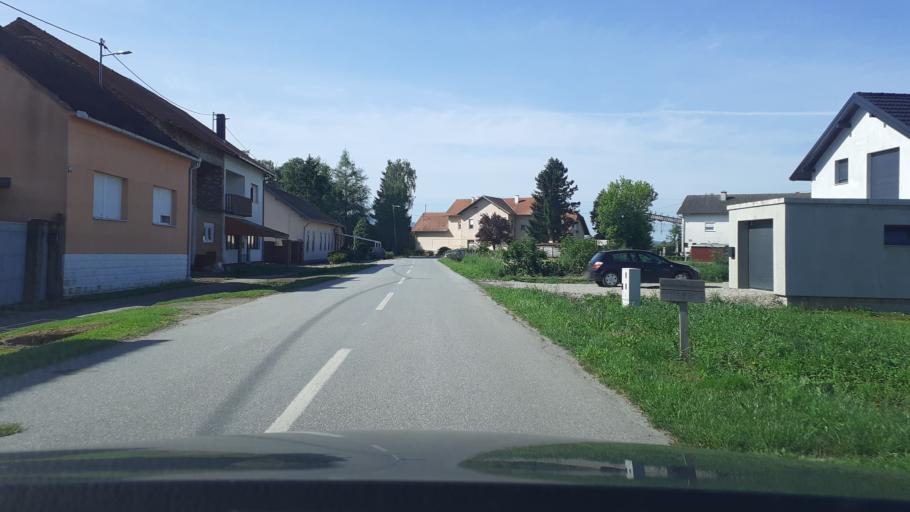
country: HR
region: Brodsko-Posavska
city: Batrina
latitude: 45.1913
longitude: 17.6507
